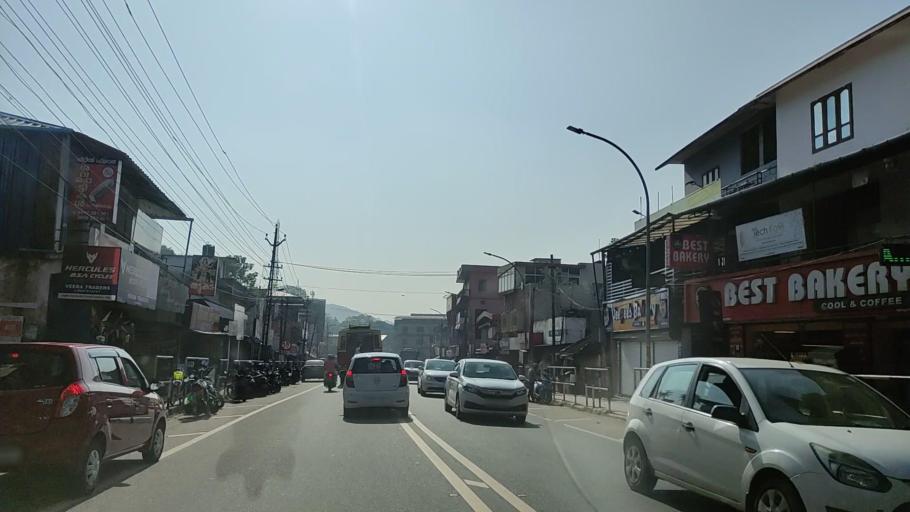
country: IN
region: Kerala
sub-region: Kollam
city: Punalur
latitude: 8.8994
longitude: 76.8588
